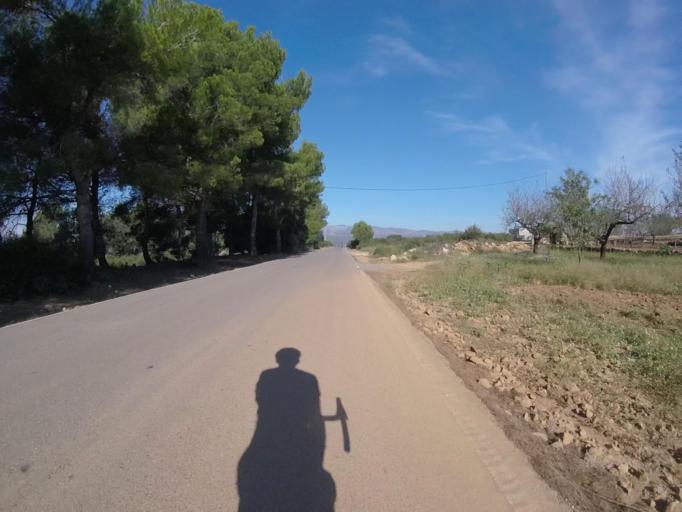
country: ES
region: Valencia
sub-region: Provincia de Castello
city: Benlloch
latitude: 40.2373
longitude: 0.0731
